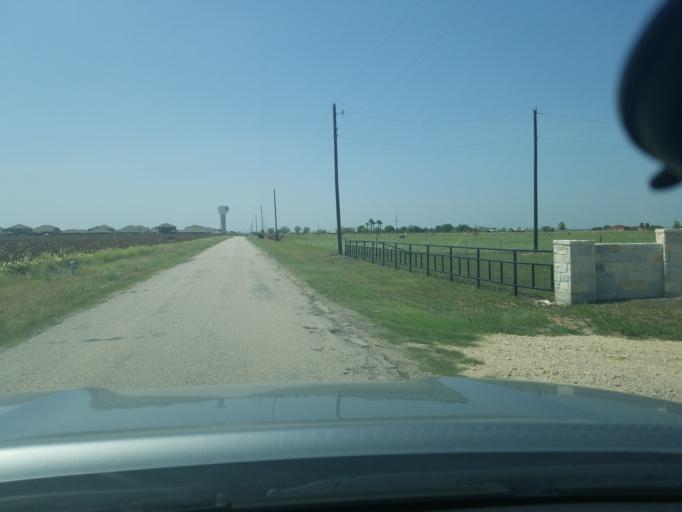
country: US
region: Texas
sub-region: Guadalupe County
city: Lake Dunlap
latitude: 29.6713
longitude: -98.0292
